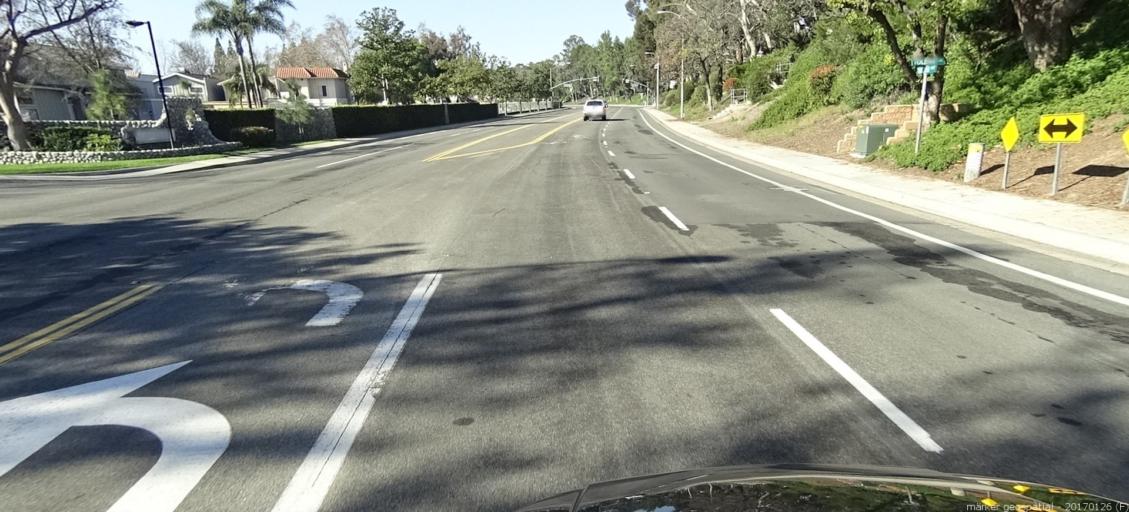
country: US
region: California
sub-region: Orange County
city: Lake Forest
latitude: 33.6456
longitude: -117.7017
